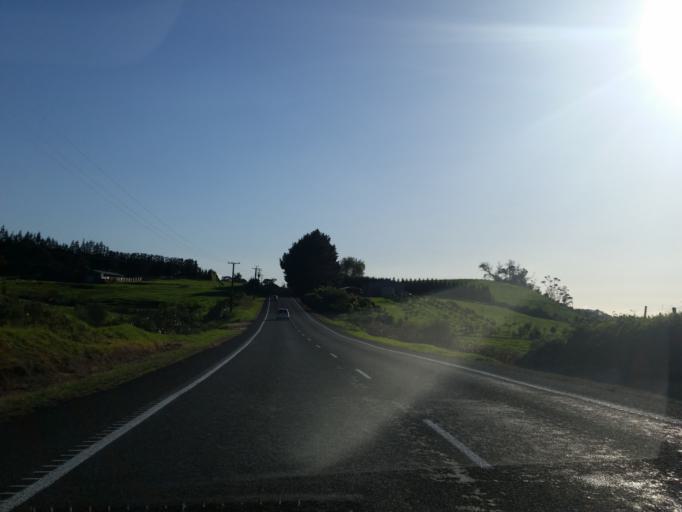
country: NZ
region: Bay of Plenty
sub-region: Western Bay of Plenty District
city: Waihi Beach
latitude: -37.4730
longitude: 175.9350
